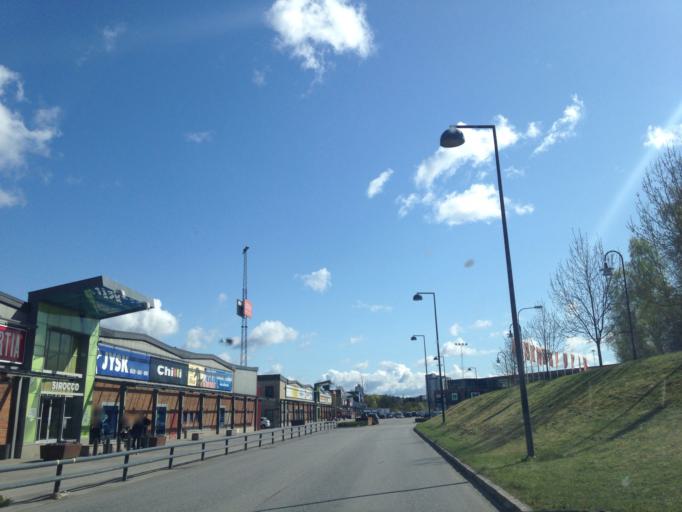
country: SE
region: Stockholm
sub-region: Nacka Kommun
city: Nacka
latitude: 59.3048
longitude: 18.1247
